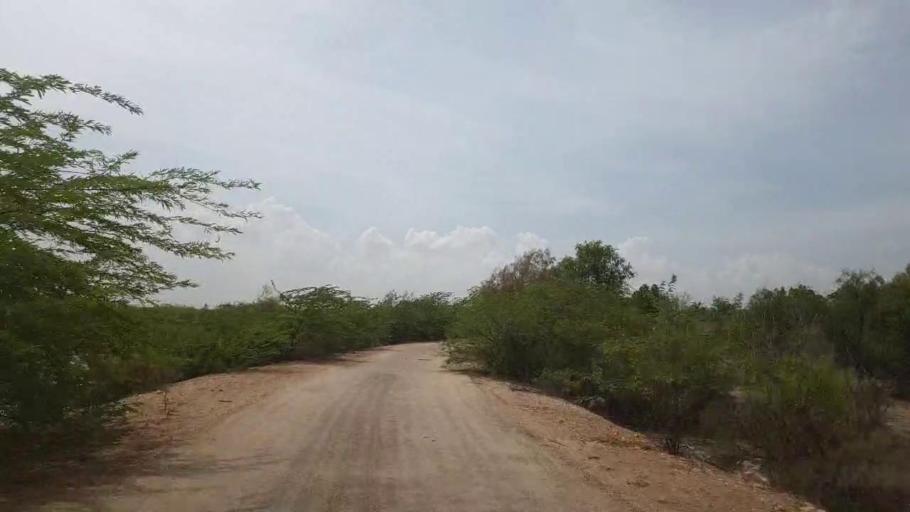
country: PK
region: Sindh
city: Kot Diji
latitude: 27.2375
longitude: 69.0798
